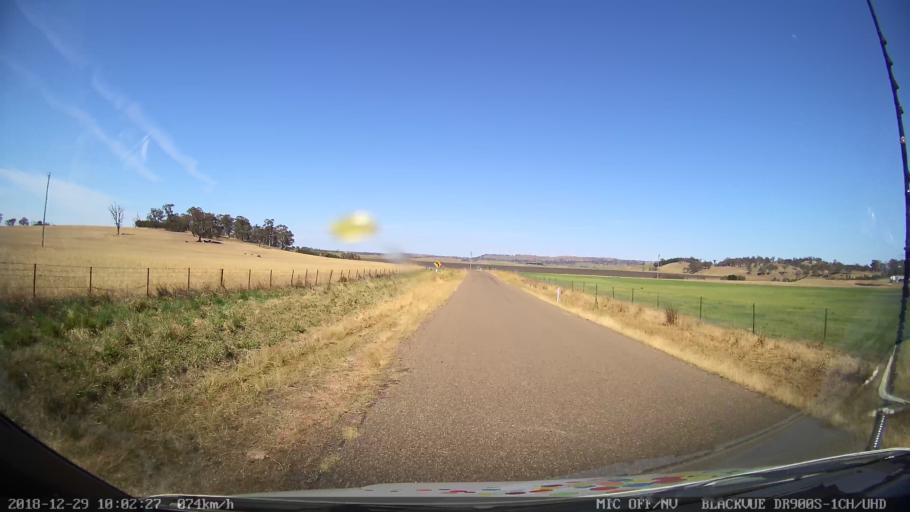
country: AU
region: New South Wales
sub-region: Goulburn Mulwaree
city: Goulburn
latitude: -34.8016
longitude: 149.4641
